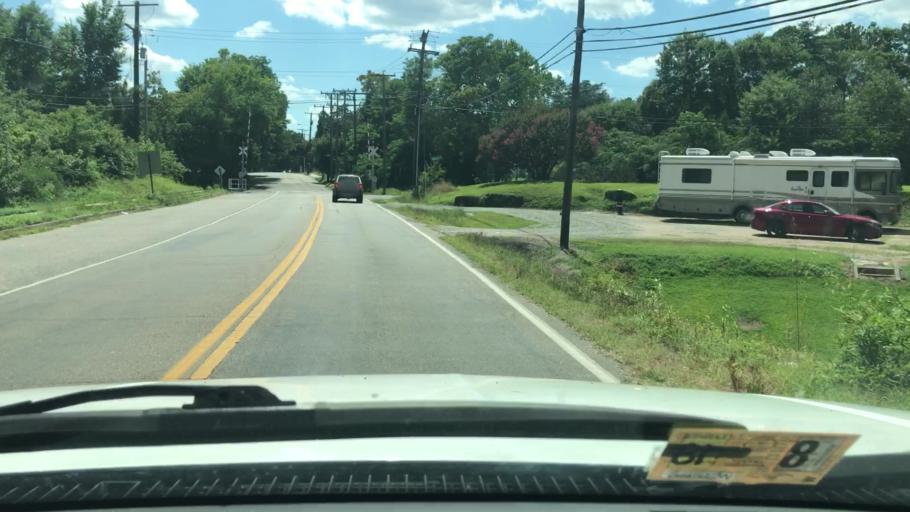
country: US
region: Virginia
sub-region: Henrico County
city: East Highland Park
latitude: 37.5731
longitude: -77.4097
